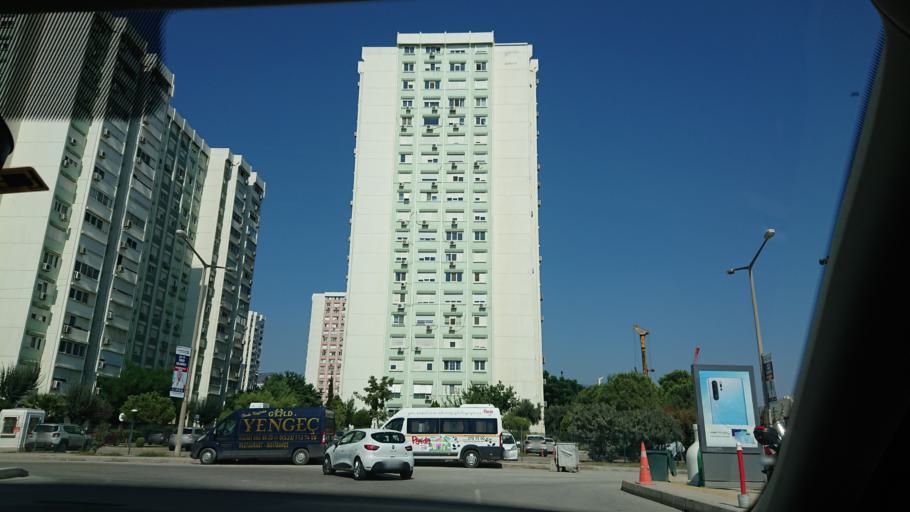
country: TR
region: Izmir
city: Karsiyaka
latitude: 38.4680
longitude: 27.0811
